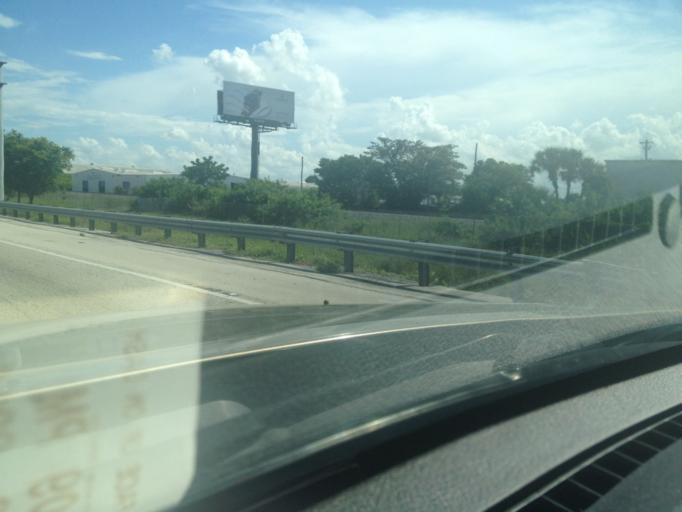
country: US
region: Florida
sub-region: Broward County
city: Roosevelt Gardens
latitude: 26.1426
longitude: -80.1699
